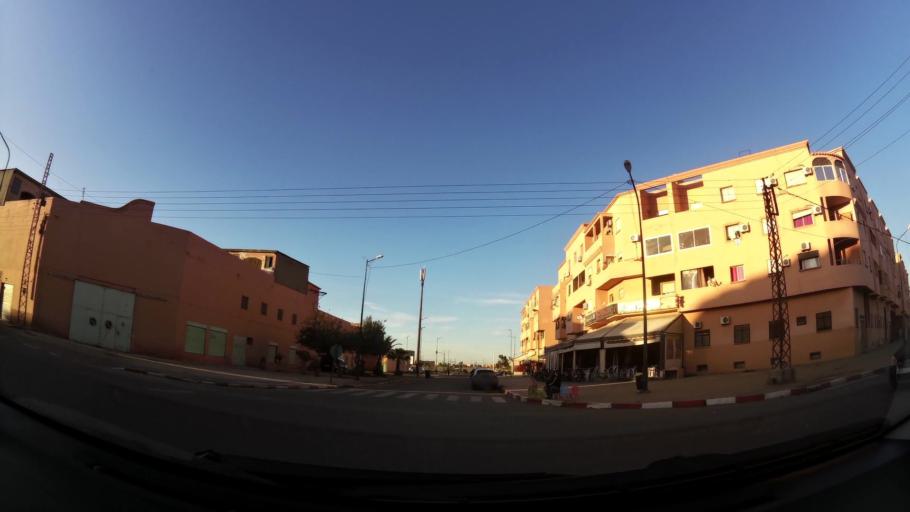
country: MA
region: Marrakech-Tensift-Al Haouz
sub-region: Marrakech
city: Marrakesh
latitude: 31.6254
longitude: -8.0287
